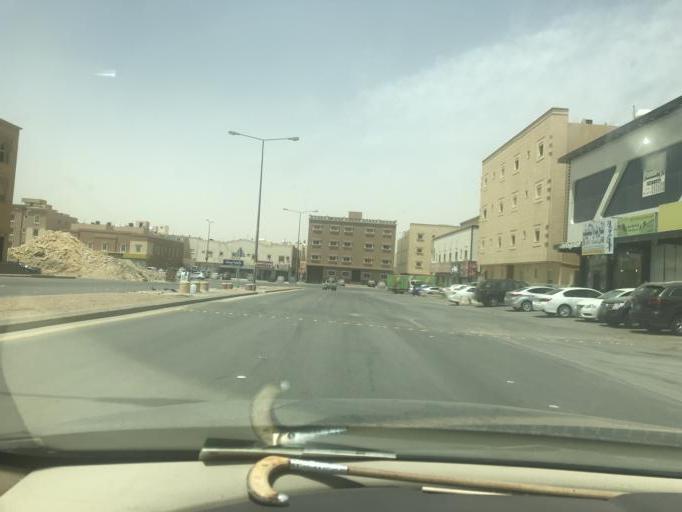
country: SA
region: Ar Riyad
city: Riyadh
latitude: 24.7986
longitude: 46.6663
